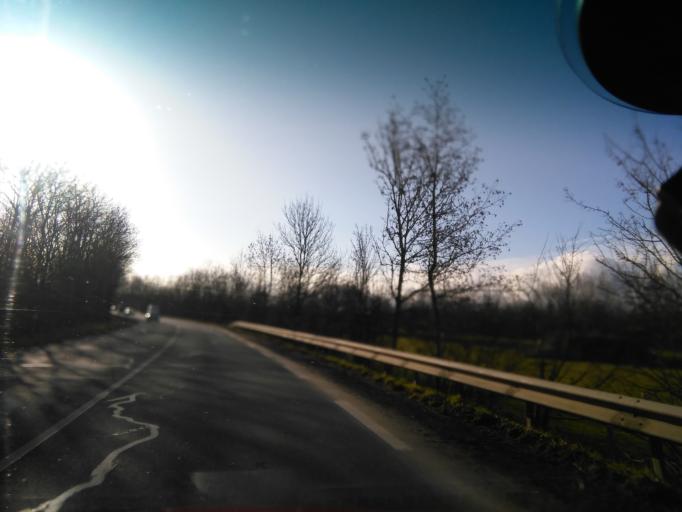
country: FR
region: Lower Normandy
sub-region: Departement du Calvados
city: Louvigny
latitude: 49.1658
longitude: -0.3879
